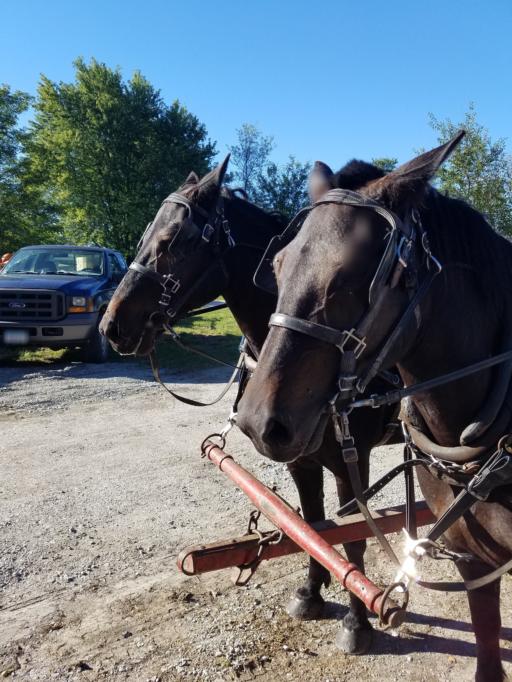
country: US
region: Iowa
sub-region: Decatur County
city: Lamoni
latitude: 40.6308
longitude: -93.8951
